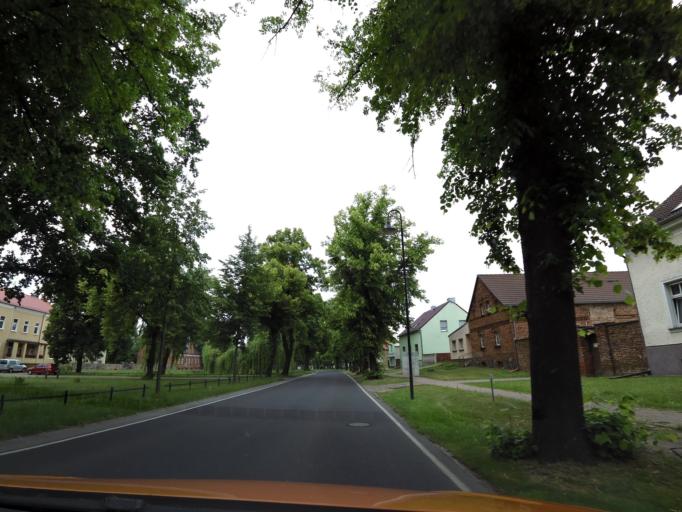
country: DE
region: Brandenburg
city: Rangsdorf
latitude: 52.2503
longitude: 13.3807
